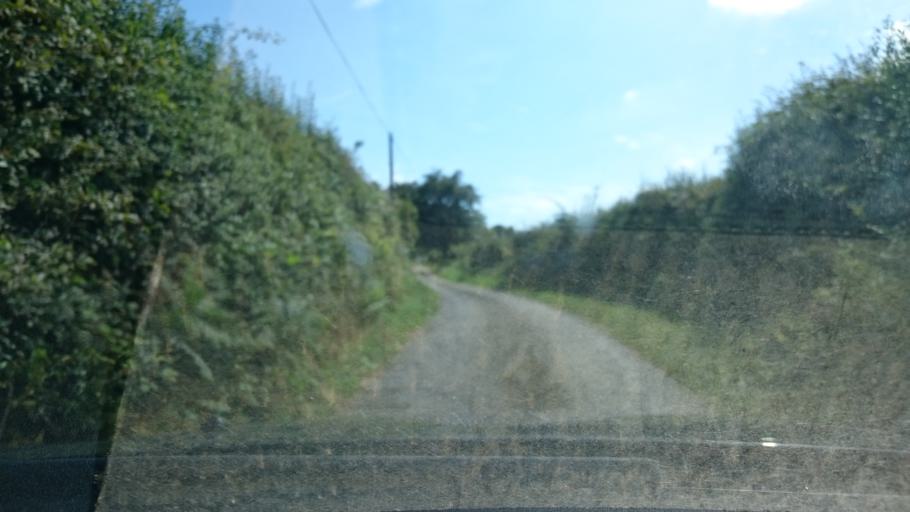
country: IE
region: Leinster
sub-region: Kilkenny
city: Graiguenamanagh
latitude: 52.5336
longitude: -6.9652
